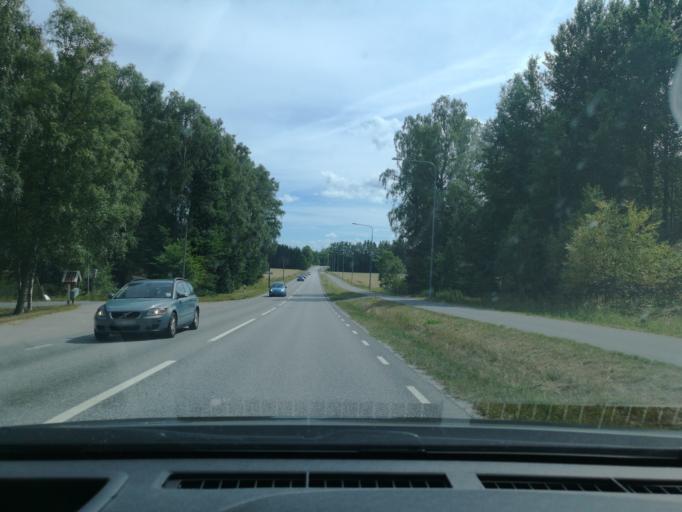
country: SE
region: Stockholm
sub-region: Sigtuna Kommun
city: Rosersberg
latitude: 59.5975
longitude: 17.8841
